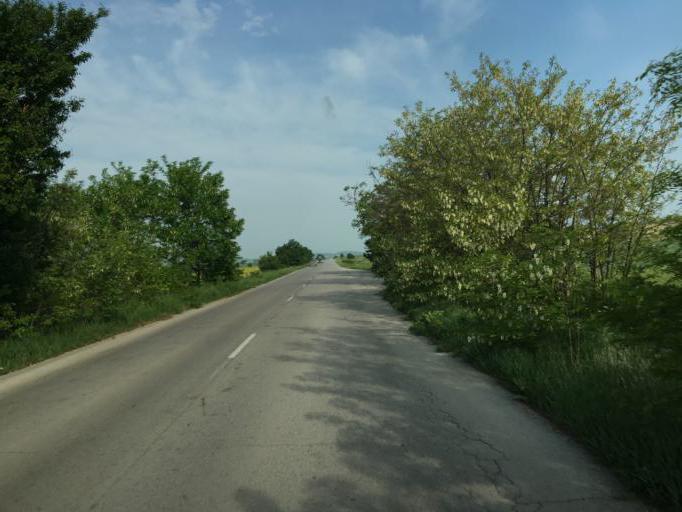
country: BG
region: Kyustendil
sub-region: Obshtina Bobovdol
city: Bobovdol
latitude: 42.4643
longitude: 23.0845
